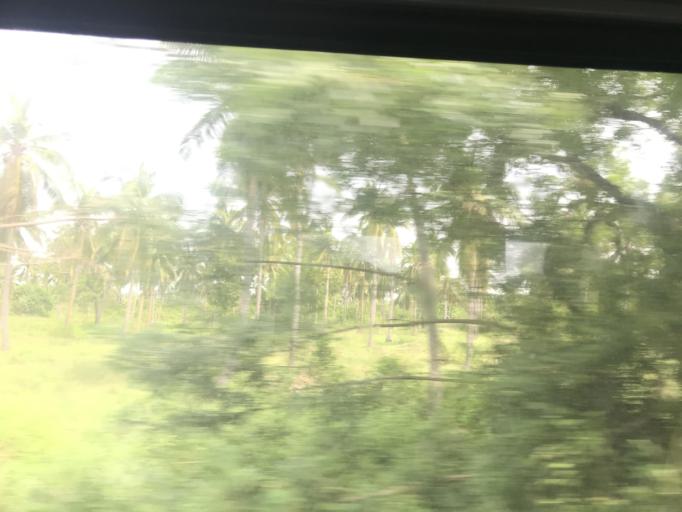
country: LK
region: Northern Province
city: Kilinochchi
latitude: 9.5794
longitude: 80.3546
